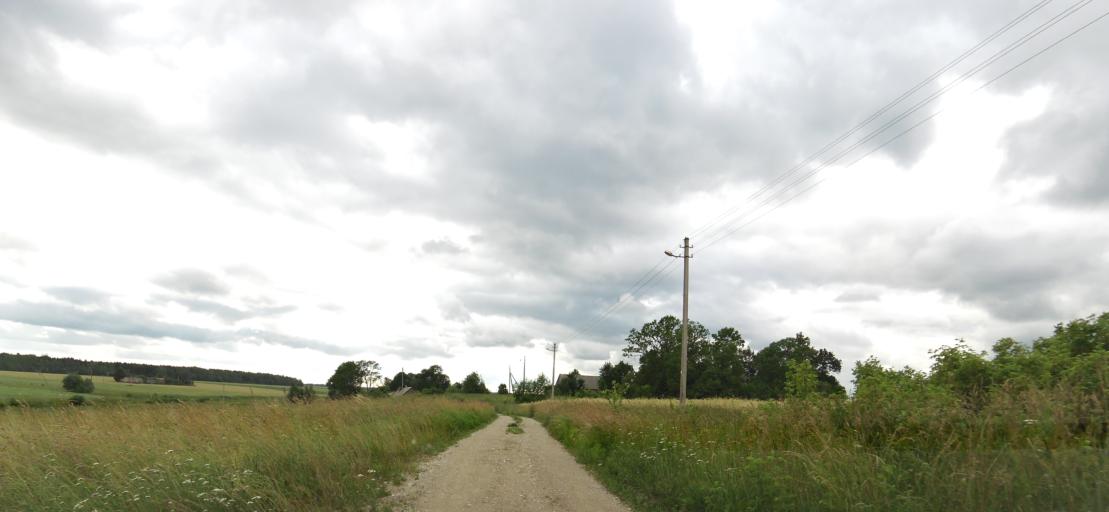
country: LT
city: Obeliai
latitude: 56.0703
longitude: 25.1055
